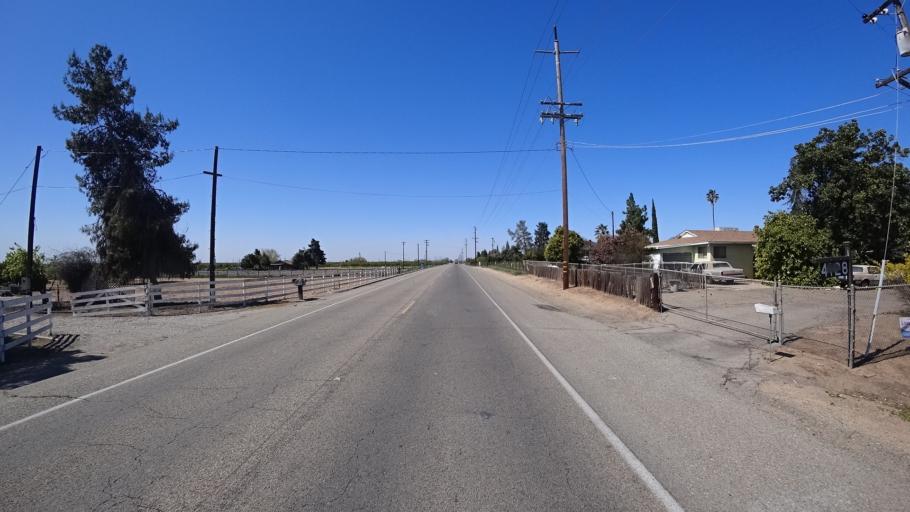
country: US
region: California
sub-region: Fresno County
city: West Park
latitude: 36.7065
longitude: -119.8648
